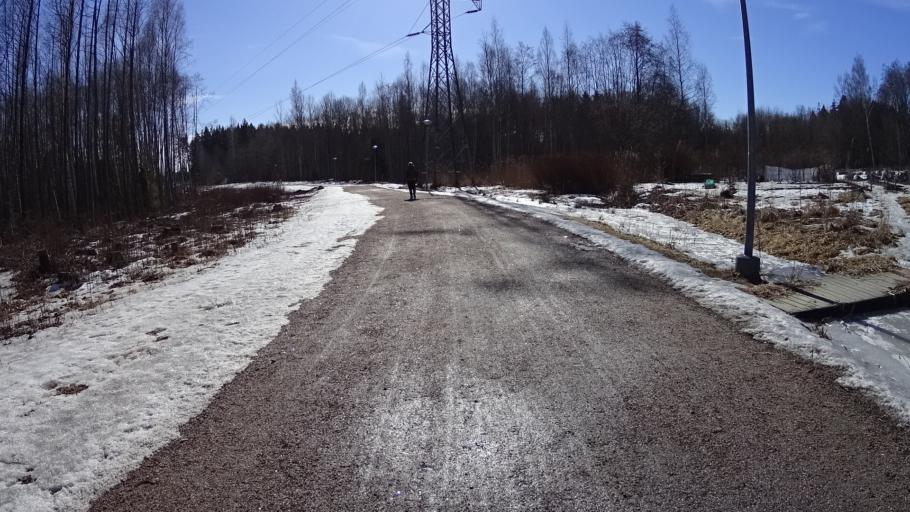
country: FI
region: Uusimaa
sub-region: Helsinki
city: Kilo
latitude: 60.2604
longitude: 24.7945
